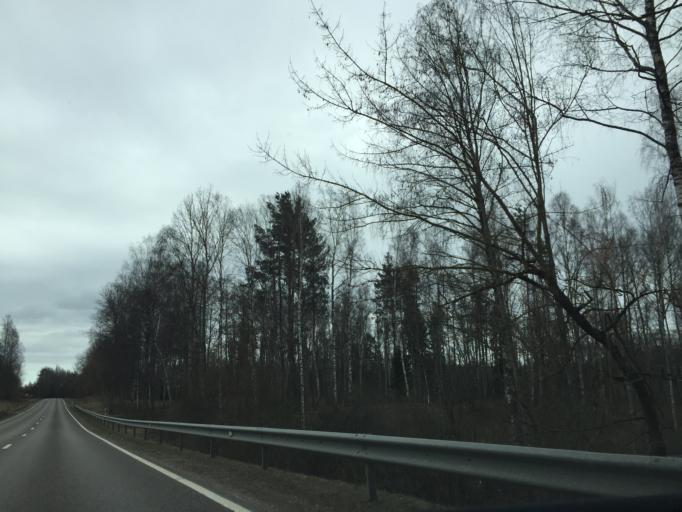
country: LV
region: Kraslavas Rajons
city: Kraslava
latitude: 55.9028
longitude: 27.1130
